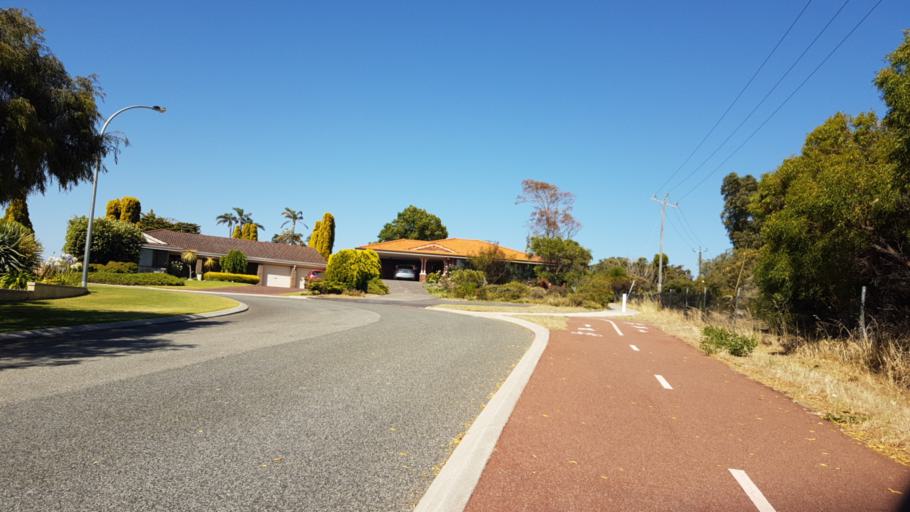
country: AU
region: Western Australia
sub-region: Stirling
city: Karrinyup
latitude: -31.8571
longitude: 115.7714
